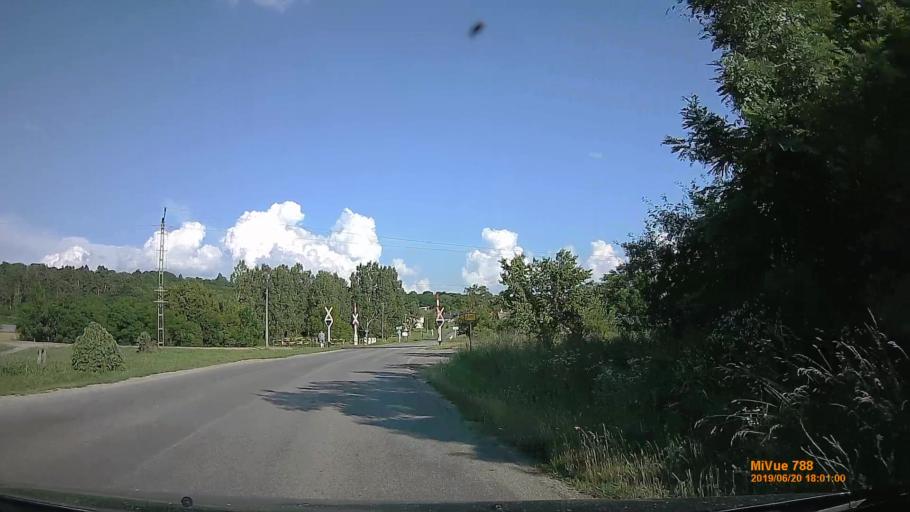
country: HU
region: Baranya
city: Buekkoesd
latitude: 46.0856
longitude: 17.9869
